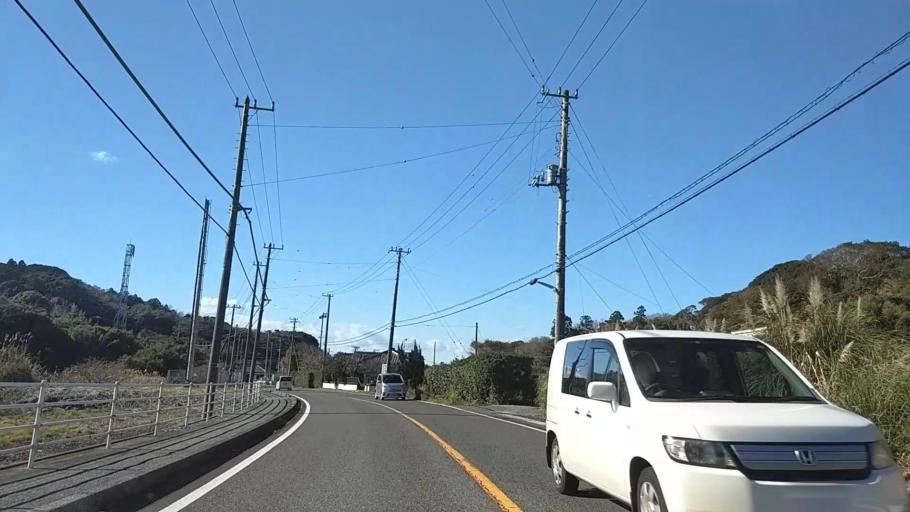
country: JP
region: Chiba
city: Tateyama
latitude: 34.9526
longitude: 139.8404
